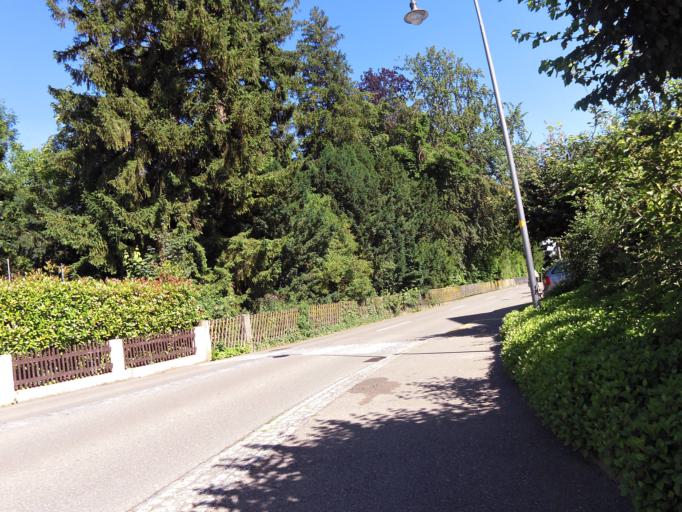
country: CH
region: Thurgau
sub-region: Kreuzlingen District
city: Gottlieben
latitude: 47.6601
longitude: 9.1347
